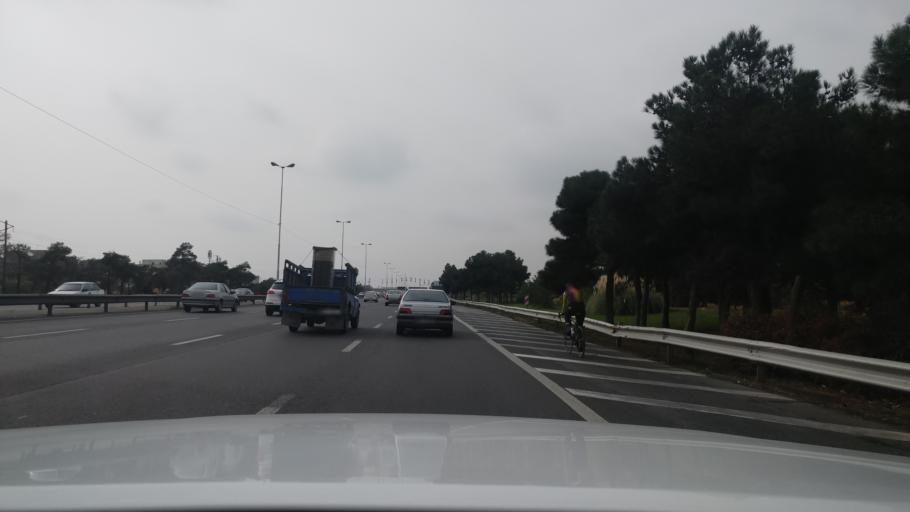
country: IR
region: Tehran
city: Tehran
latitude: 35.7155
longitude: 51.2722
